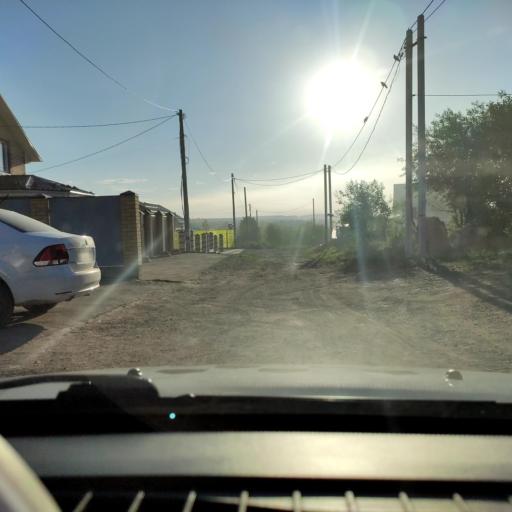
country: RU
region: Perm
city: Perm
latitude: 58.0203
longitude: 56.3371
